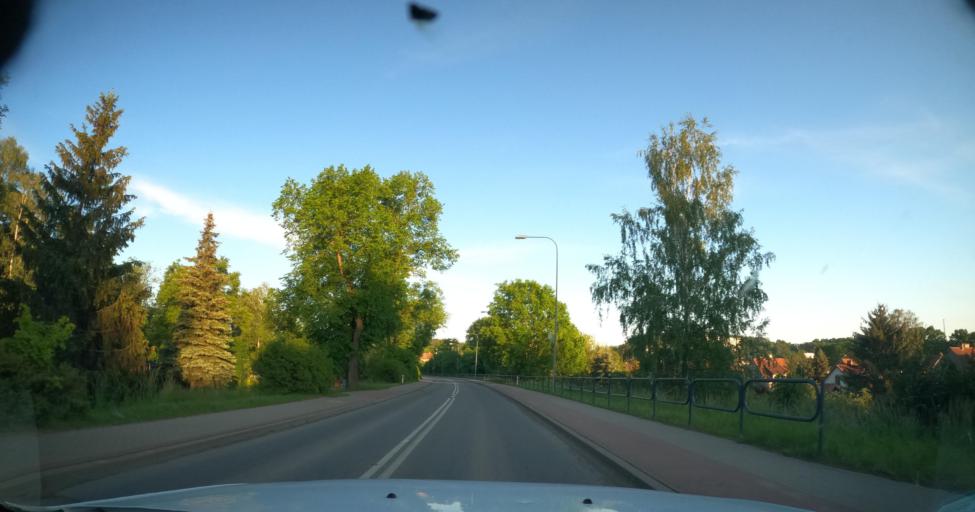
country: PL
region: Warmian-Masurian Voivodeship
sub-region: Powiat lidzbarski
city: Lidzbark Warminski
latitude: 54.1265
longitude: 20.5673
